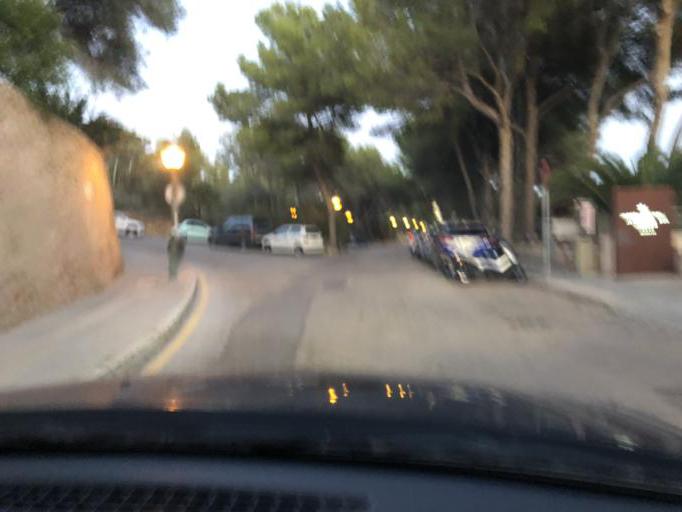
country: ES
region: Balearic Islands
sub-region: Illes Balears
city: Santa Ponsa
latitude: 39.5200
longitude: 2.4691
